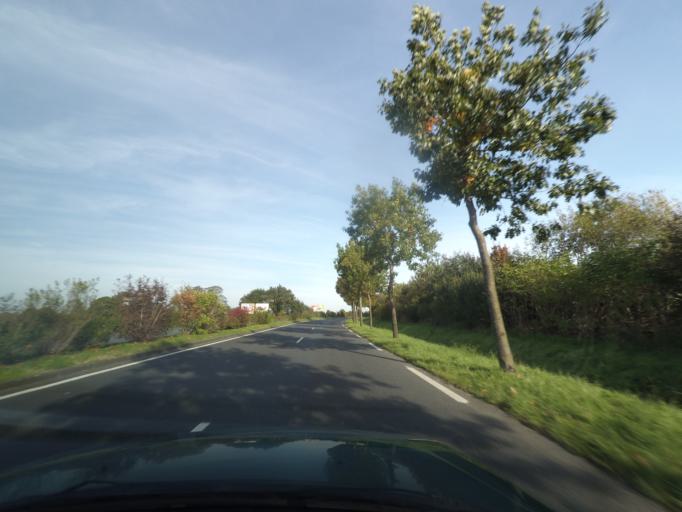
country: FR
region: Pays de la Loire
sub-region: Departement de Maine-et-Loire
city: Cholet
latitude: 47.0646
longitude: -0.9056
